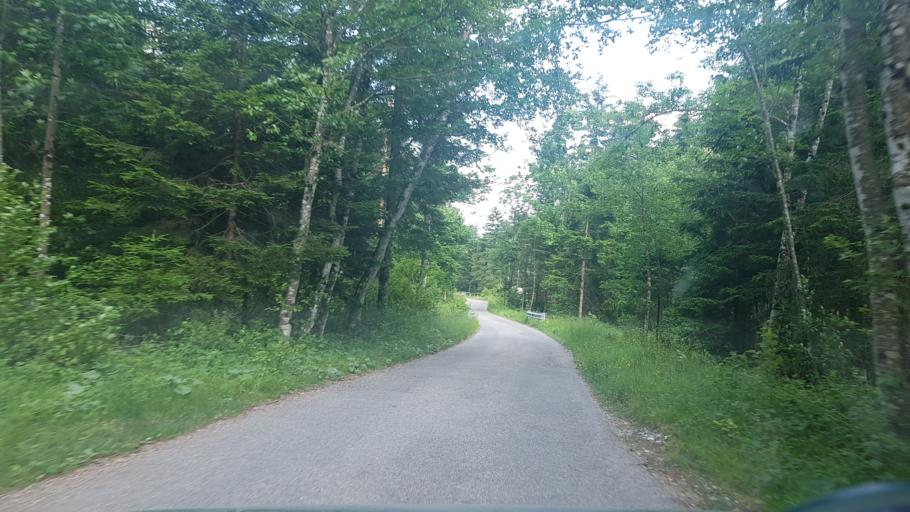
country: IT
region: Friuli Venezia Giulia
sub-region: Provincia di Udine
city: Pontebba
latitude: 46.5268
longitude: 13.2440
